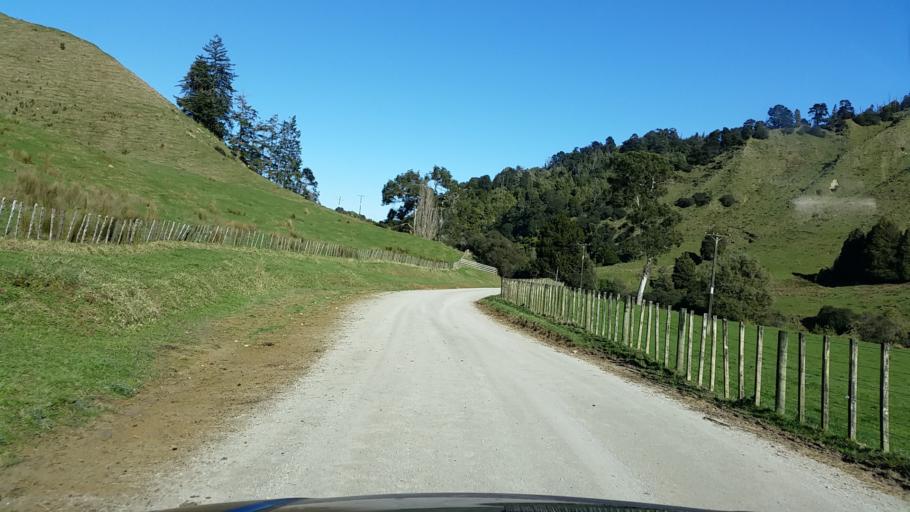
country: NZ
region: Manawatu-Wanganui
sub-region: Wanganui District
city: Wanganui
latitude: -39.5476
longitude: 174.8997
